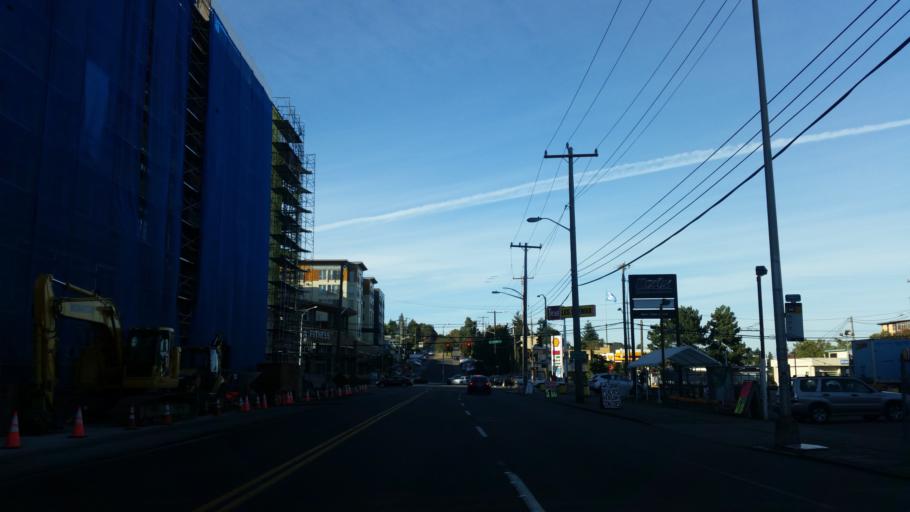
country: US
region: Washington
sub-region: King County
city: White Center
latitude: 47.5602
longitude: -122.3814
